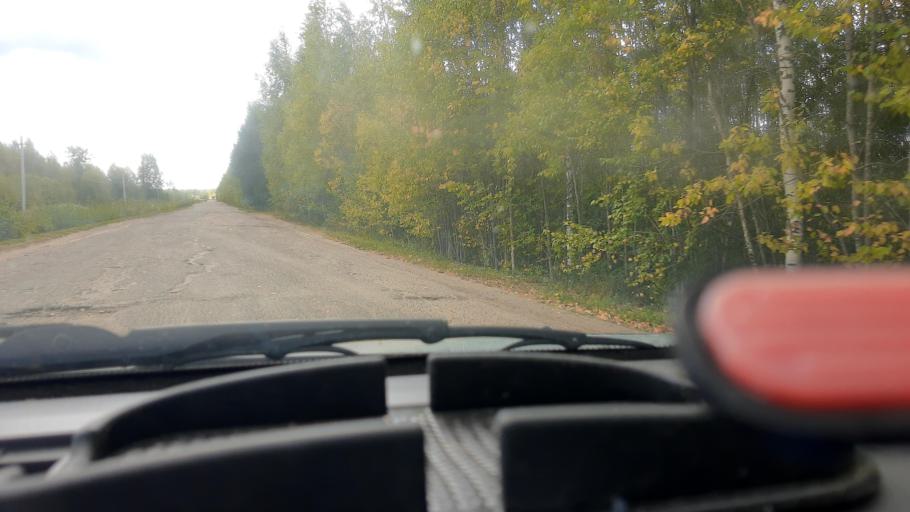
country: RU
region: Mariy-El
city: Kilemary
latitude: 56.8922
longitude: 46.7542
